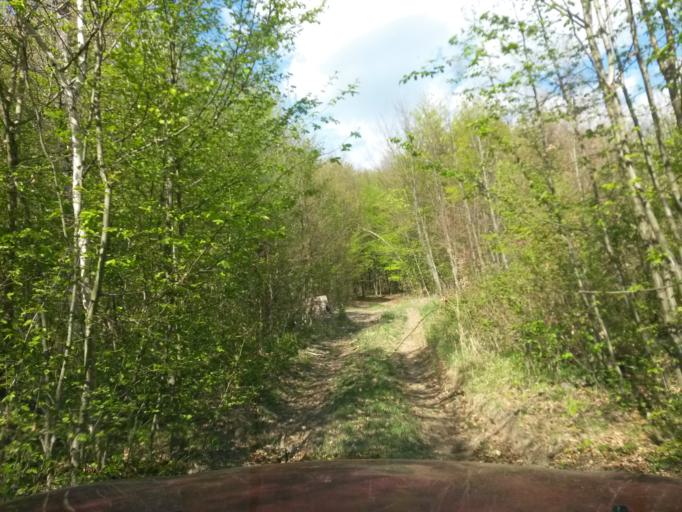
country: SK
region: Presovsky
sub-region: Okres Presov
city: Presov
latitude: 48.9492
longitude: 21.1364
